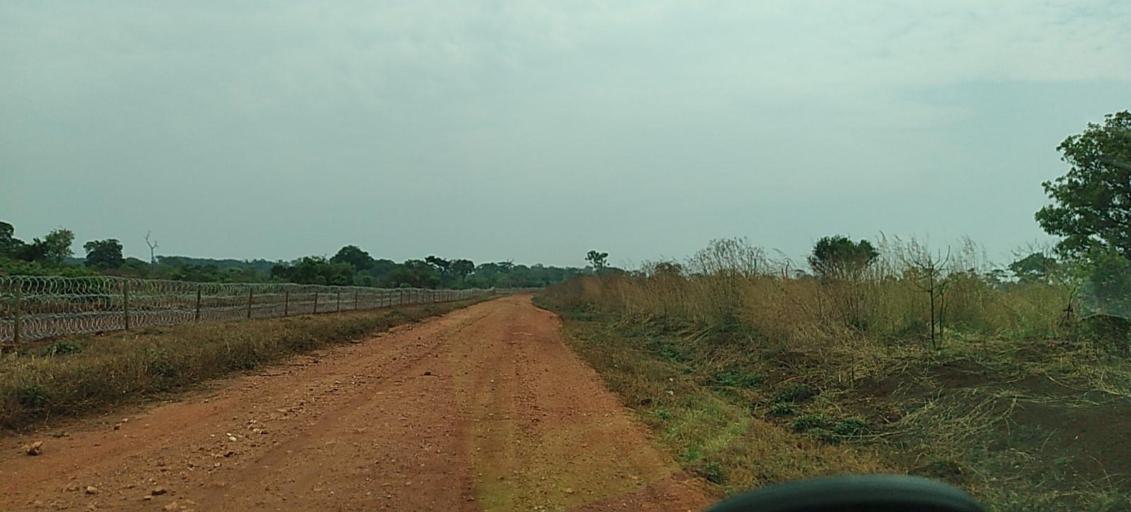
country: ZM
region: North-Western
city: Kansanshi
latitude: -12.1039
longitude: 26.4907
